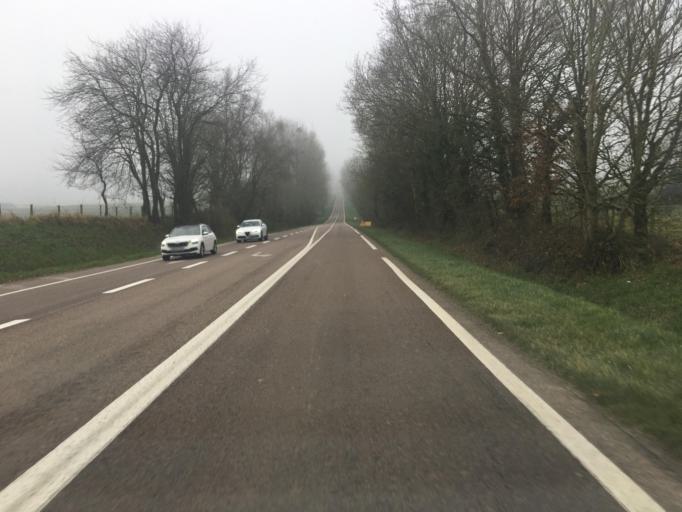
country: FR
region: Haute-Normandie
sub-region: Departement de la Seine-Maritime
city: La Remuee
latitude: 49.5402
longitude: 0.4279
